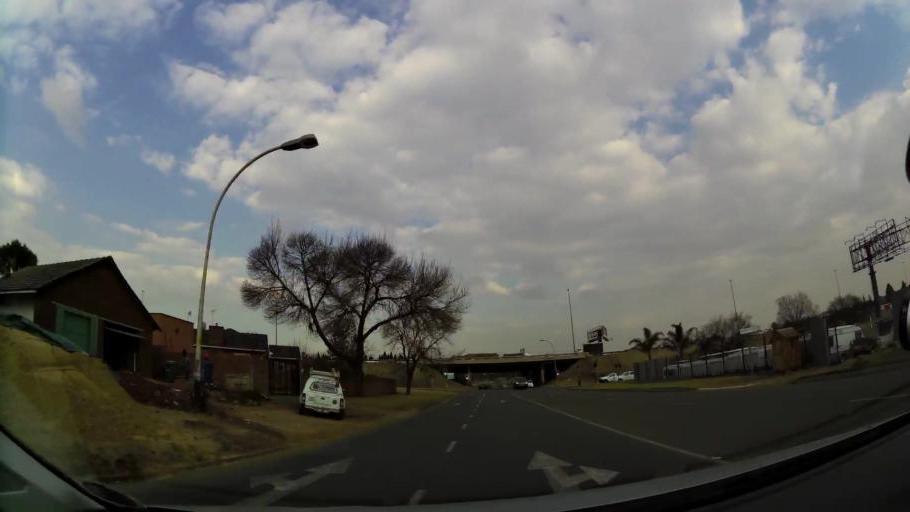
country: ZA
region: Gauteng
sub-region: City of Johannesburg Metropolitan Municipality
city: Modderfontein
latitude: -26.1401
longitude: 28.1897
